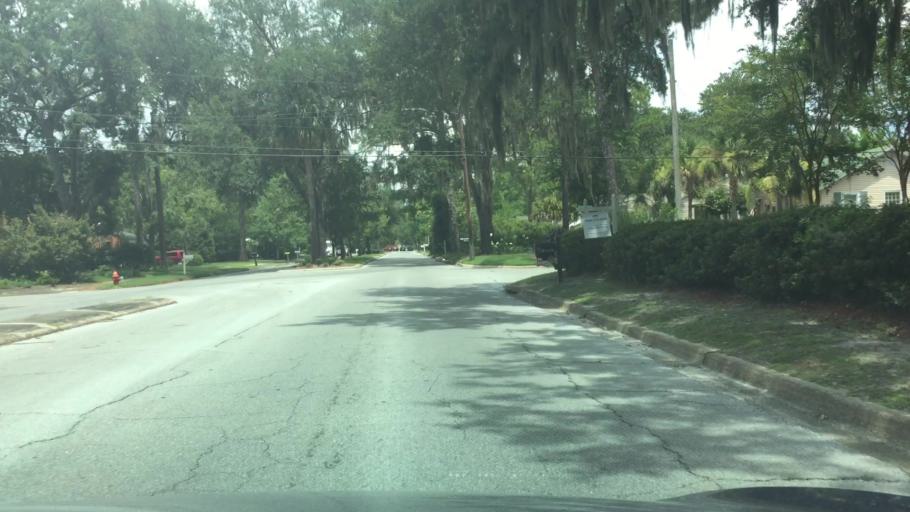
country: US
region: Florida
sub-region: Bay County
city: Panama City
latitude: 30.1474
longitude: -85.6504
